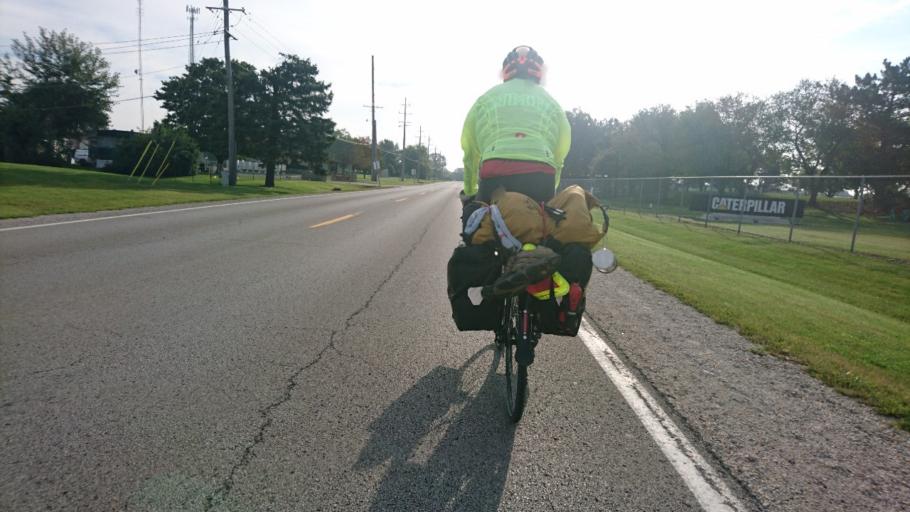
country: US
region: Illinois
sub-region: Livingston County
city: Pontiac
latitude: 40.8882
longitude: -88.6516
